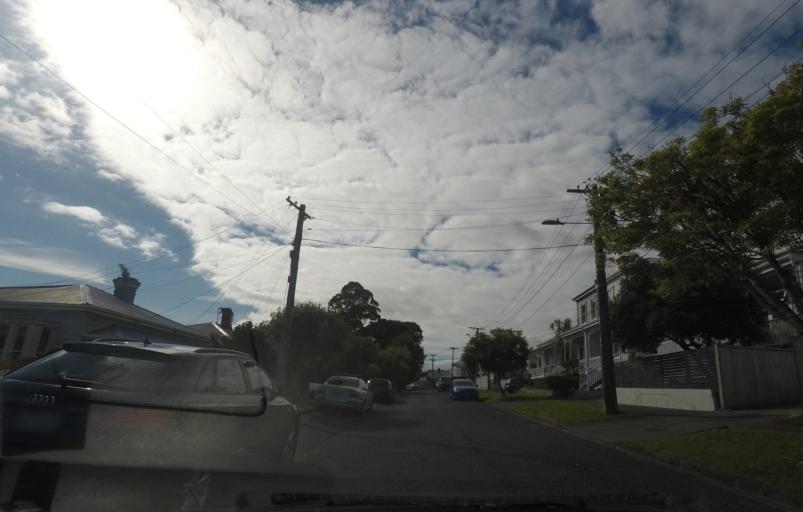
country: NZ
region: Auckland
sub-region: Auckland
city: Auckland
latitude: -36.8716
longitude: 174.7401
